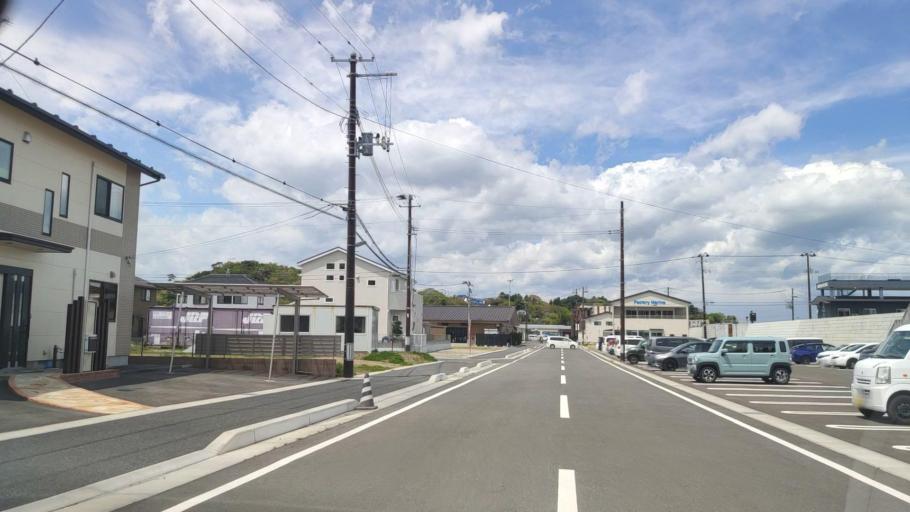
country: JP
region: Miyagi
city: Shiogama
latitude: 38.3032
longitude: 141.0848
